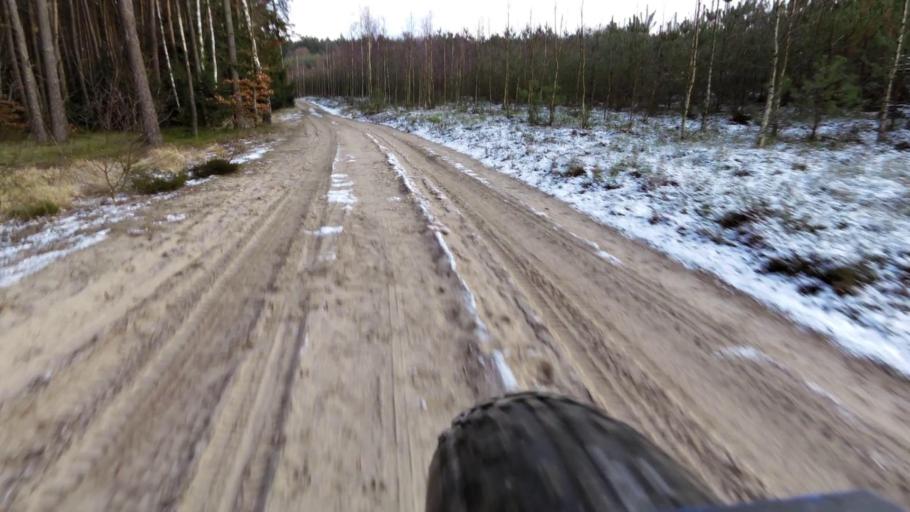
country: PL
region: West Pomeranian Voivodeship
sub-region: Powiat walecki
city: Walcz
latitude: 53.2527
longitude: 16.3631
